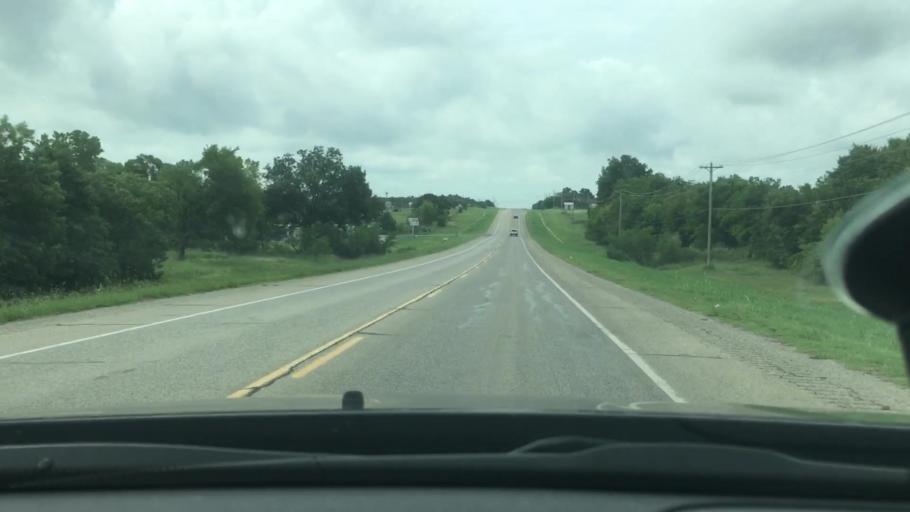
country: US
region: Oklahoma
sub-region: Carter County
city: Healdton
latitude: 34.2078
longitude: -97.4748
